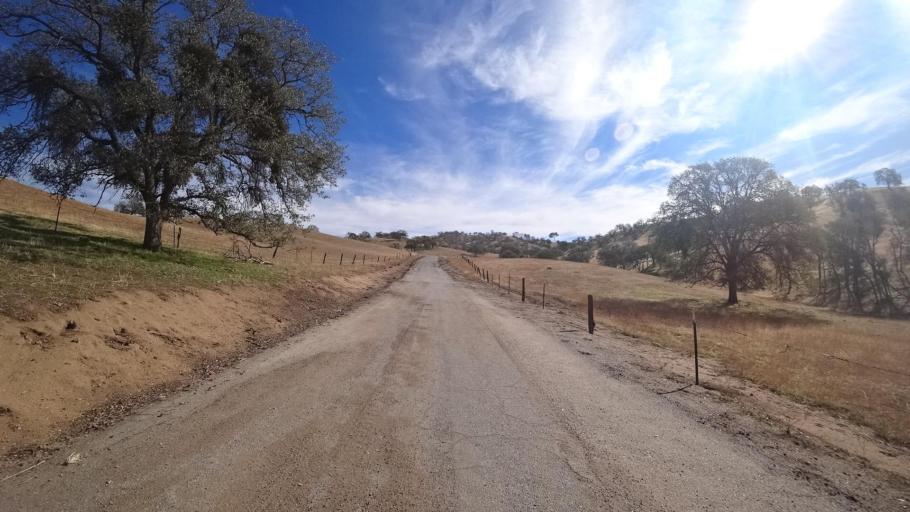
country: US
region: California
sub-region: Kern County
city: Oildale
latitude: 35.5727
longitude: -118.8035
